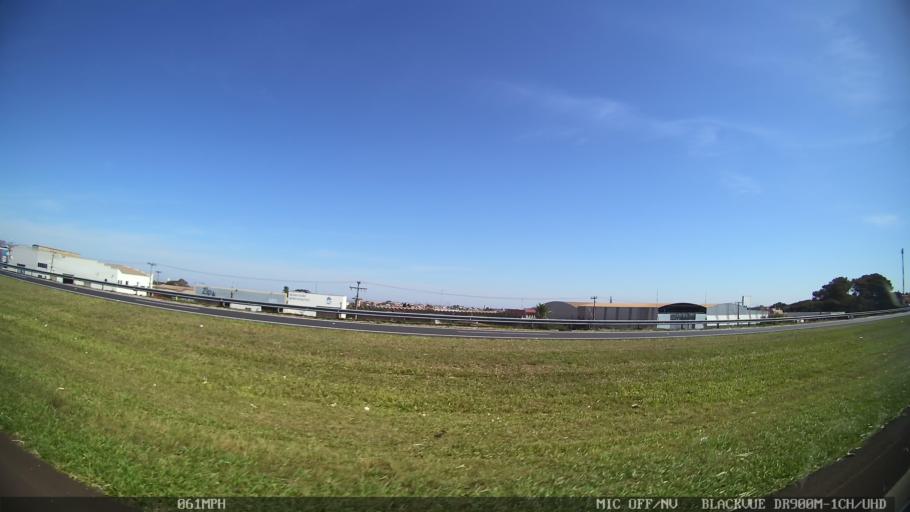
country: BR
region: Sao Paulo
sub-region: Cravinhos
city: Cravinhos
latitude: -21.3370
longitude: -47.7253
